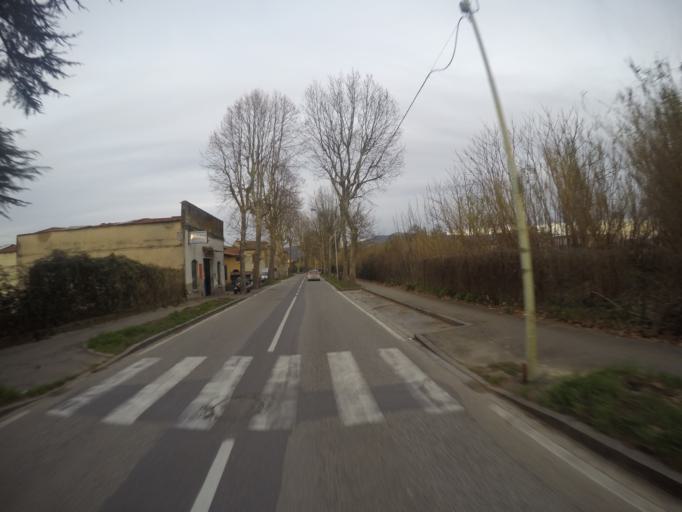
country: IT
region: Tuscany
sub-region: Provincia di Prato
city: Prato
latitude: 43.8910
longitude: 11.0599
